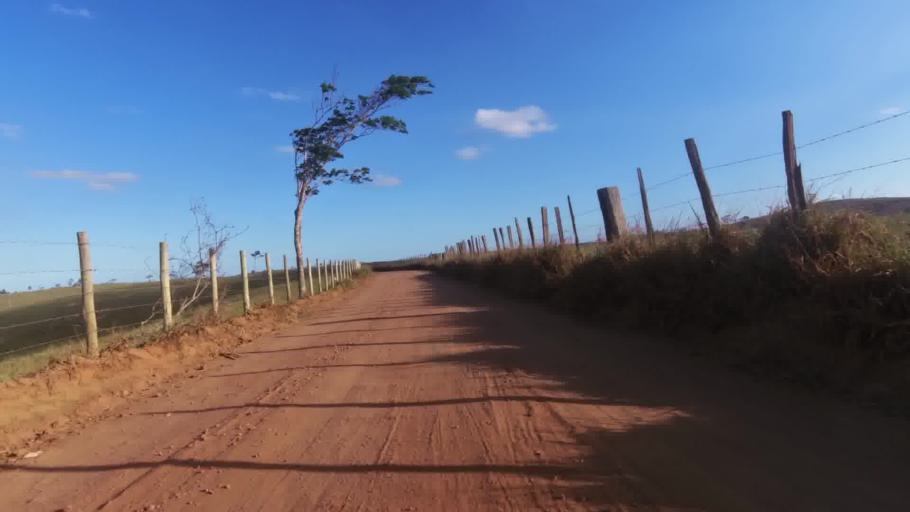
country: BR
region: Espirito Santo
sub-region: Marataizes
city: Marataizes
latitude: -21.1466
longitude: -41.0675
